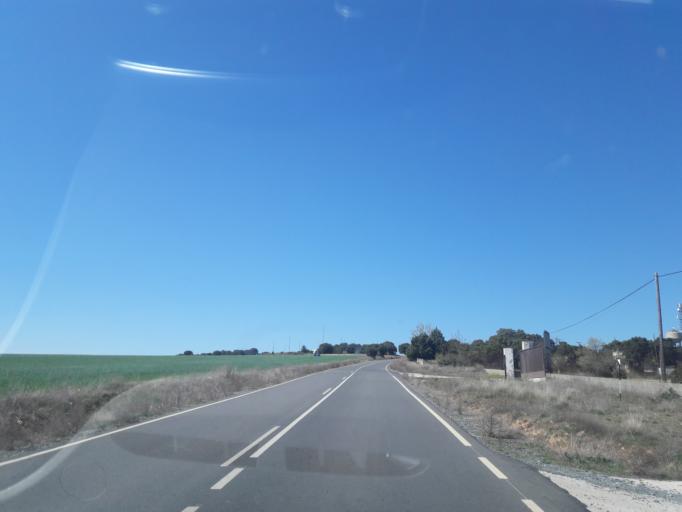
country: ES
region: Castille and Leon
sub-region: Provincia de Salamanca
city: Martinamor
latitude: 40.8106
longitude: -5.6261
